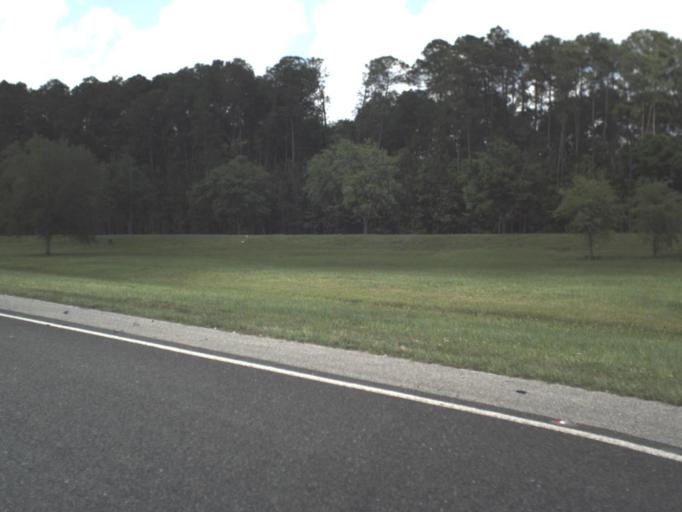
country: US
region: Florida
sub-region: Saint Johns County
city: Villano Beach
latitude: 29.9889
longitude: -81.4633
